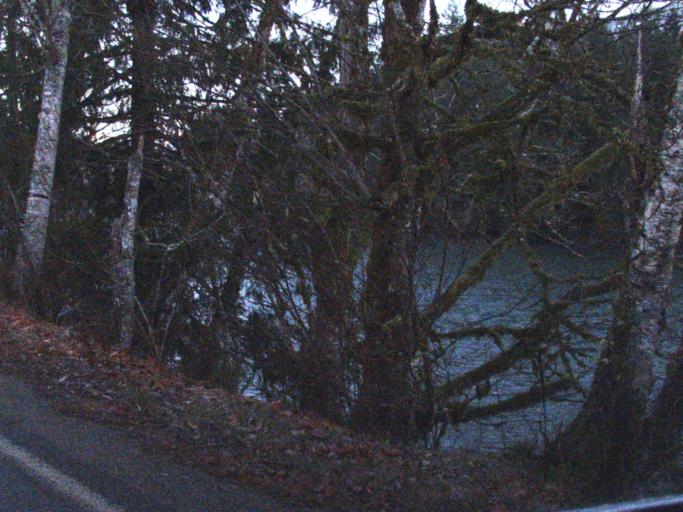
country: US
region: Washington
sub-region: Snohomish County
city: Darrington
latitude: 48.5180
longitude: -121.4648
